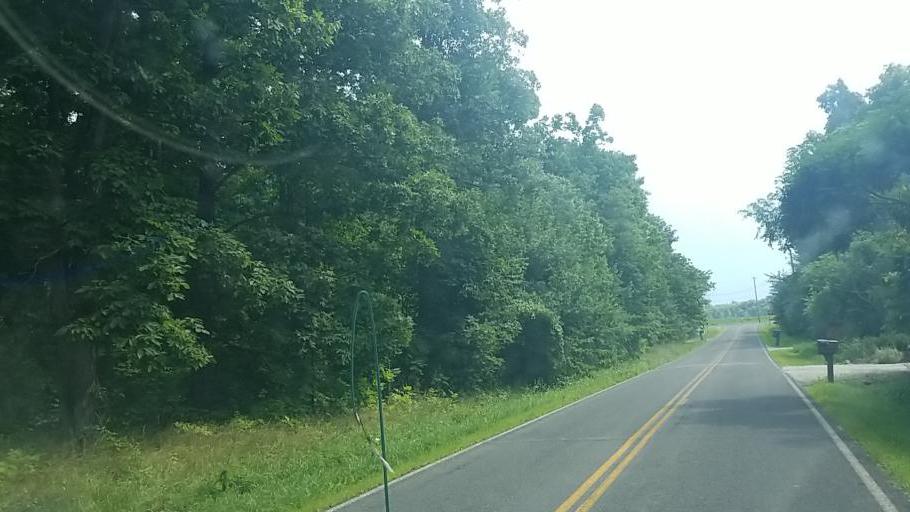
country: US
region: Ohio
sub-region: Medina County
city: Medina
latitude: 41.1374
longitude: -81.9545
